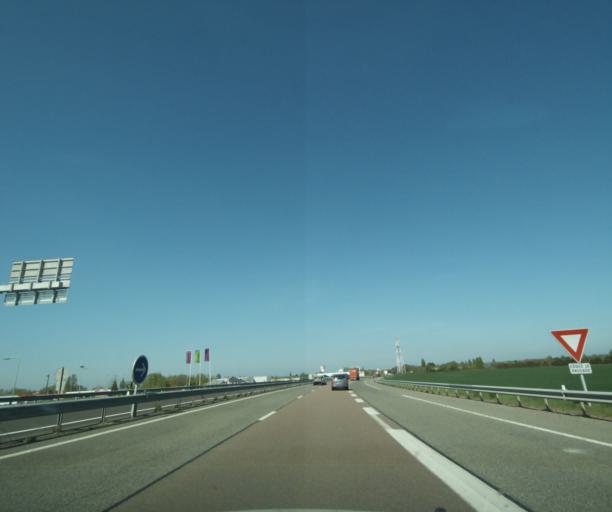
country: FR
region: Bourgogne
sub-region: Departement de la Nievre
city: Cosne-Cours-sur-Loire
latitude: 47.3860
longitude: 2.9234
